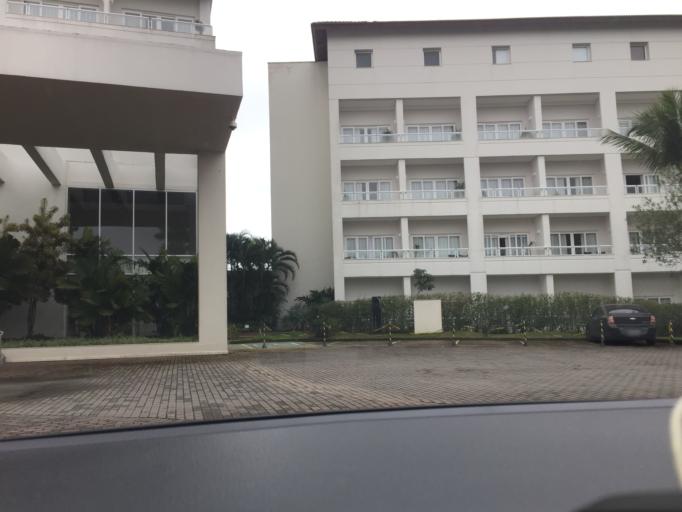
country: BR
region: Sao Paulo
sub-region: Guaruja
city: Guaruja
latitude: -23.9694
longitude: -46.1869
